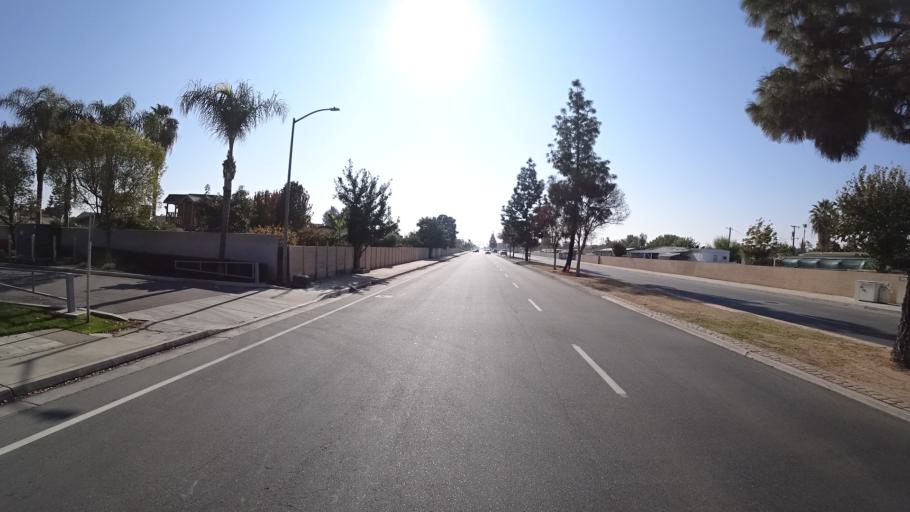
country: US
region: California
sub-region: Kern County
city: Greenfield
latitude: 35.2997
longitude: -119.0389
